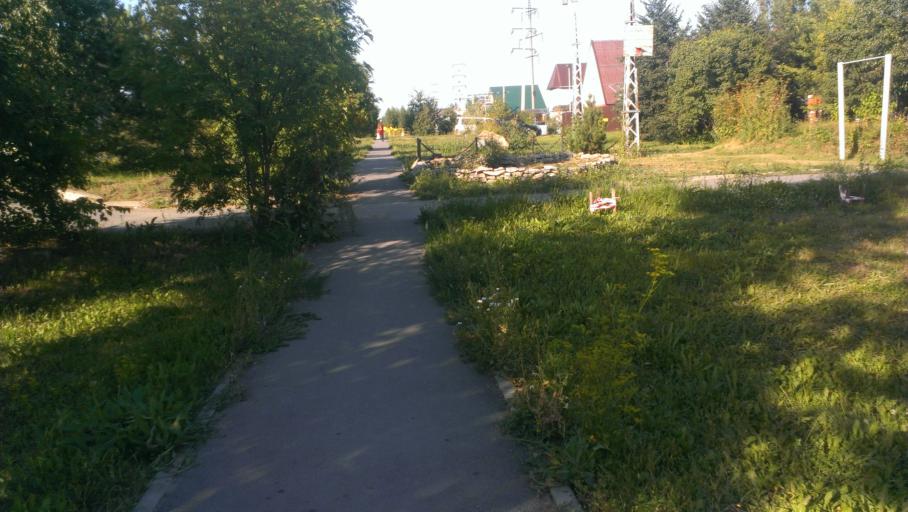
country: RU
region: Altai Krai
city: Novosilikatnyy
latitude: 53.3575
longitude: 83.6379
